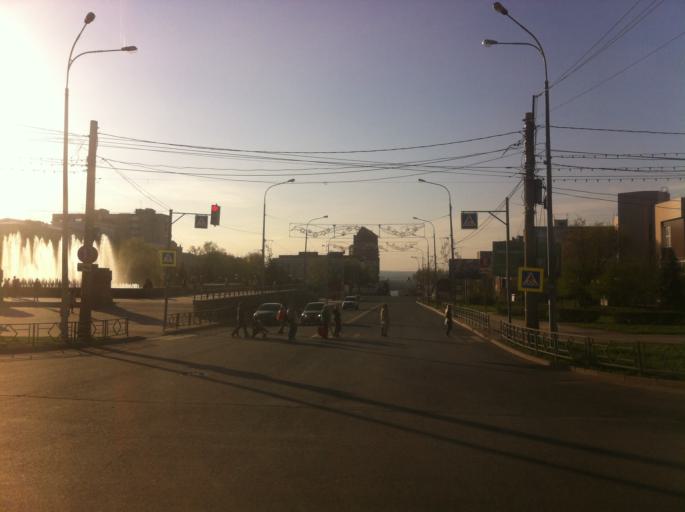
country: RU
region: Samara
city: Samara
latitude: 53.2079
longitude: 50.1355
